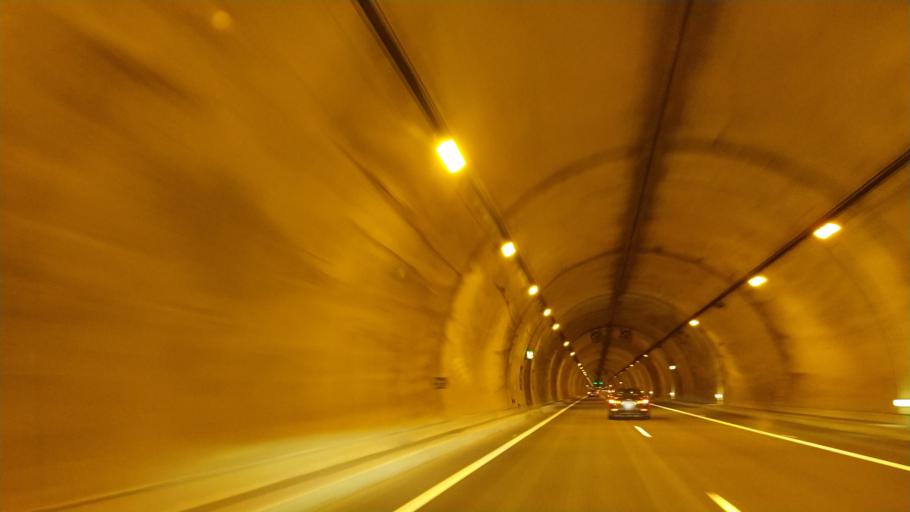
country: ES
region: Cantabria
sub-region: Provincia de Cantabria
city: Los Corrales de Buelna
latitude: 43.2283
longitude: -4.0810
